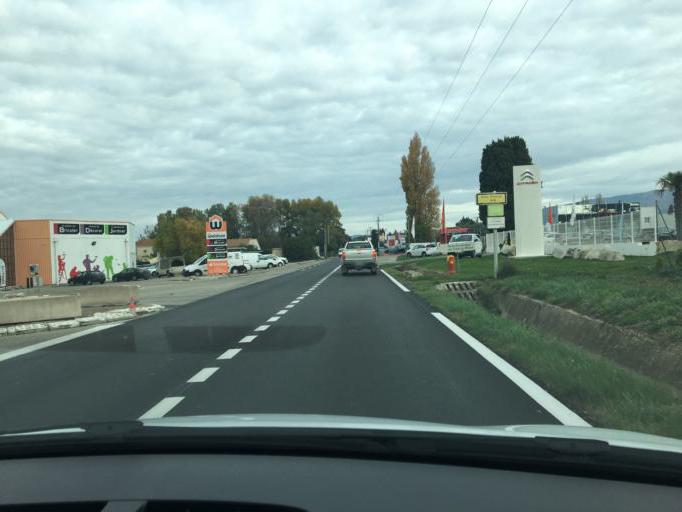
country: FR
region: Provence-Alpes-Cote d'Azur
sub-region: Departement du Vaucluse
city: Valreas
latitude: 44.3691
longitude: 4.9787
